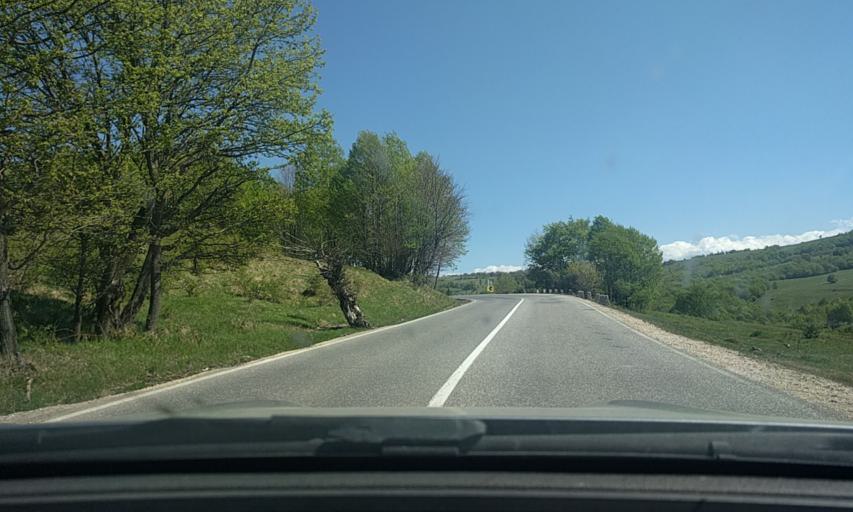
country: RO
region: Brasov
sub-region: Comuna Vama Buzaului
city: Acris
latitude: 45.6821
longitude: 25.9554
